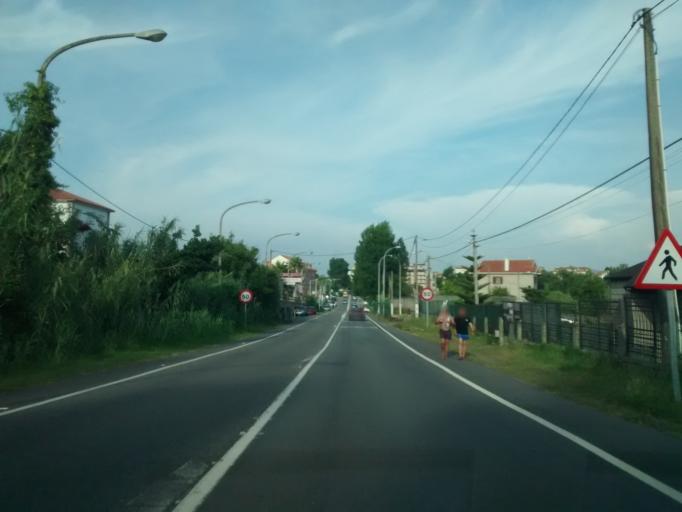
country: ES
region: Galicia
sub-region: Provincia de Pontevedra
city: Sanxenxo
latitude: 42.3920
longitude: -8.8350
